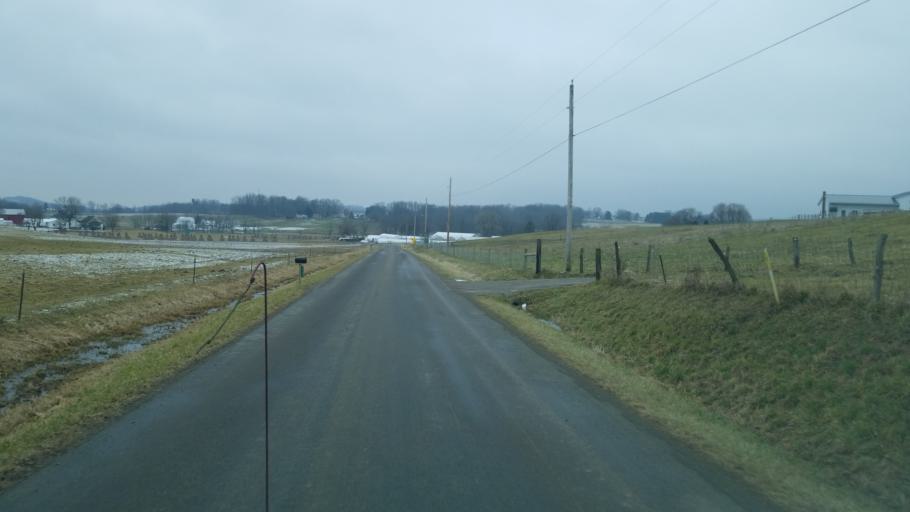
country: US
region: Ohio
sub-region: Wayne County
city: Apple Creek
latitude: 40.6964
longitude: -81.8639
